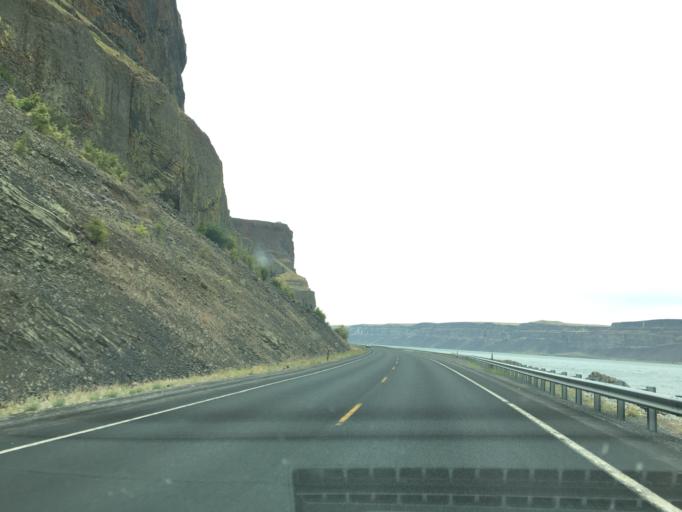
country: US
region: Washington
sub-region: Okanogan County
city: Coulee Dam
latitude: 47.8086
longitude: -119.1679
